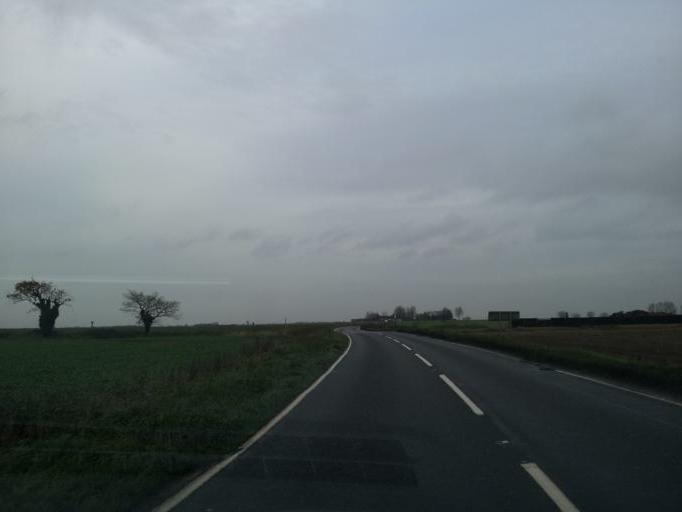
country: GB
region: England
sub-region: Norfolk
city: Martham
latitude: 52.6780
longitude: 1.5944
